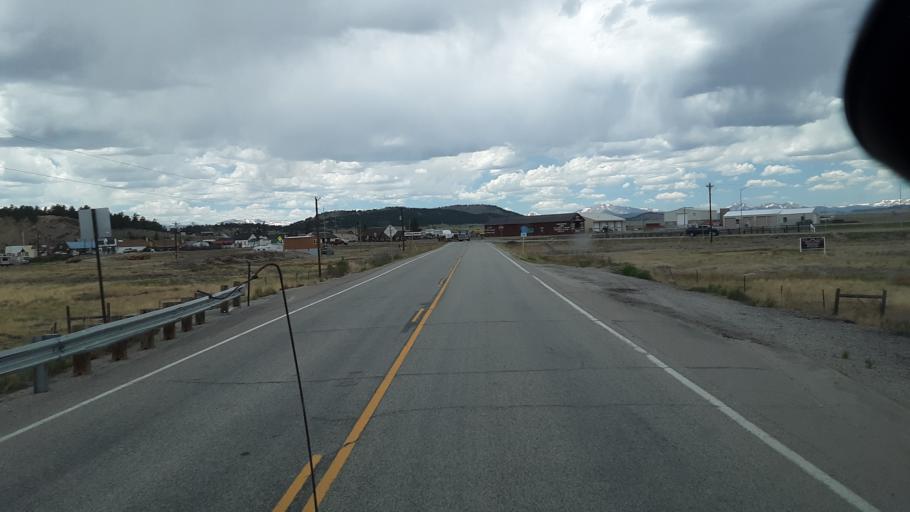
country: US
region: Colorado
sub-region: Park County
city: Fairplay
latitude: 39.0200
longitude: -105.7923
